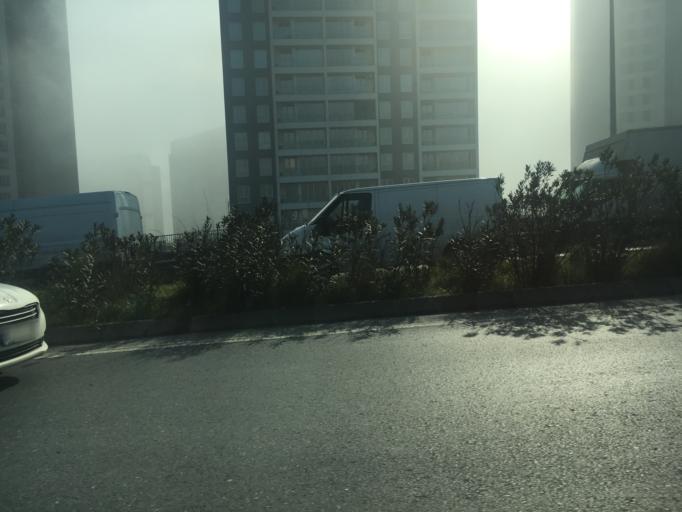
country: TR
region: Istanbul
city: Esenyurt
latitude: 41.0544
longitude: 28.6843
